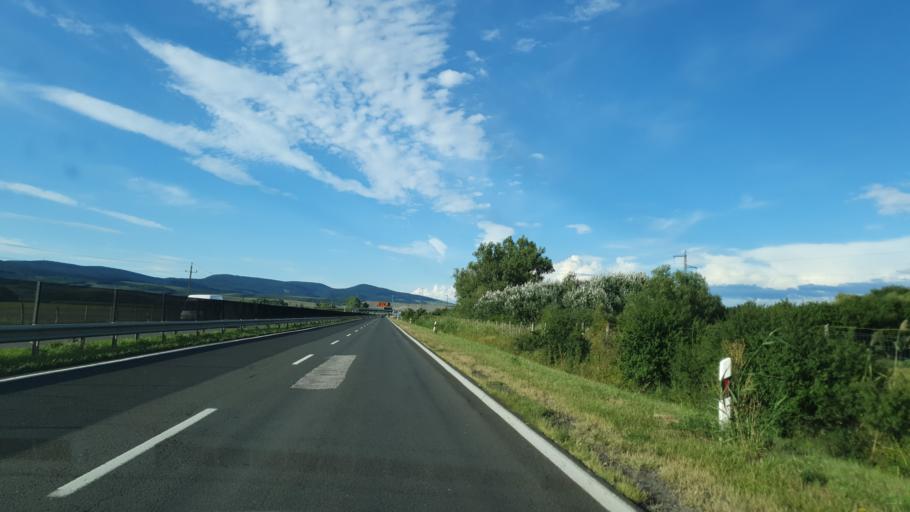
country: HU
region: Nograd
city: Paszto
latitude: 47.9152
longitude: 19.6834
